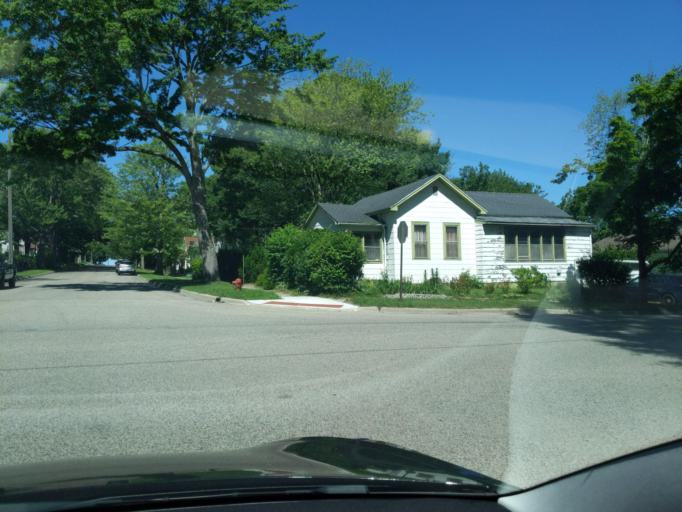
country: US
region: Michigan
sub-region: Muskegon County
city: Muskegon
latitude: 43.2267
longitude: -86.2683
